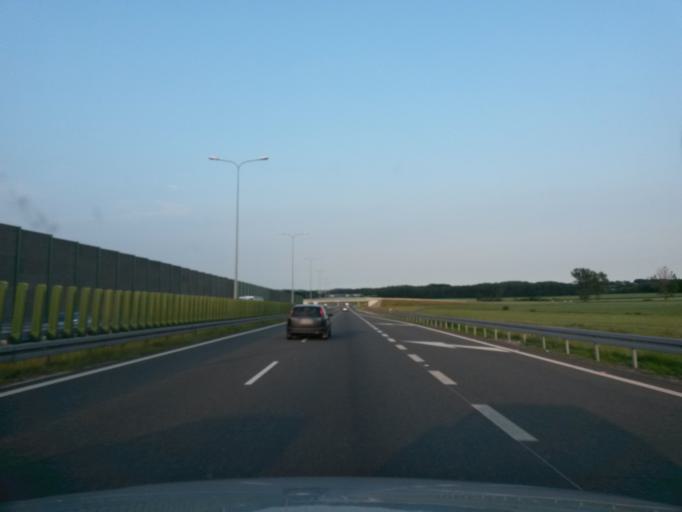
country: PL
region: Lower Silesian Voivodeship
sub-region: Powiat olesnicki
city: Sycow
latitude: 51.2952
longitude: 17.6845
